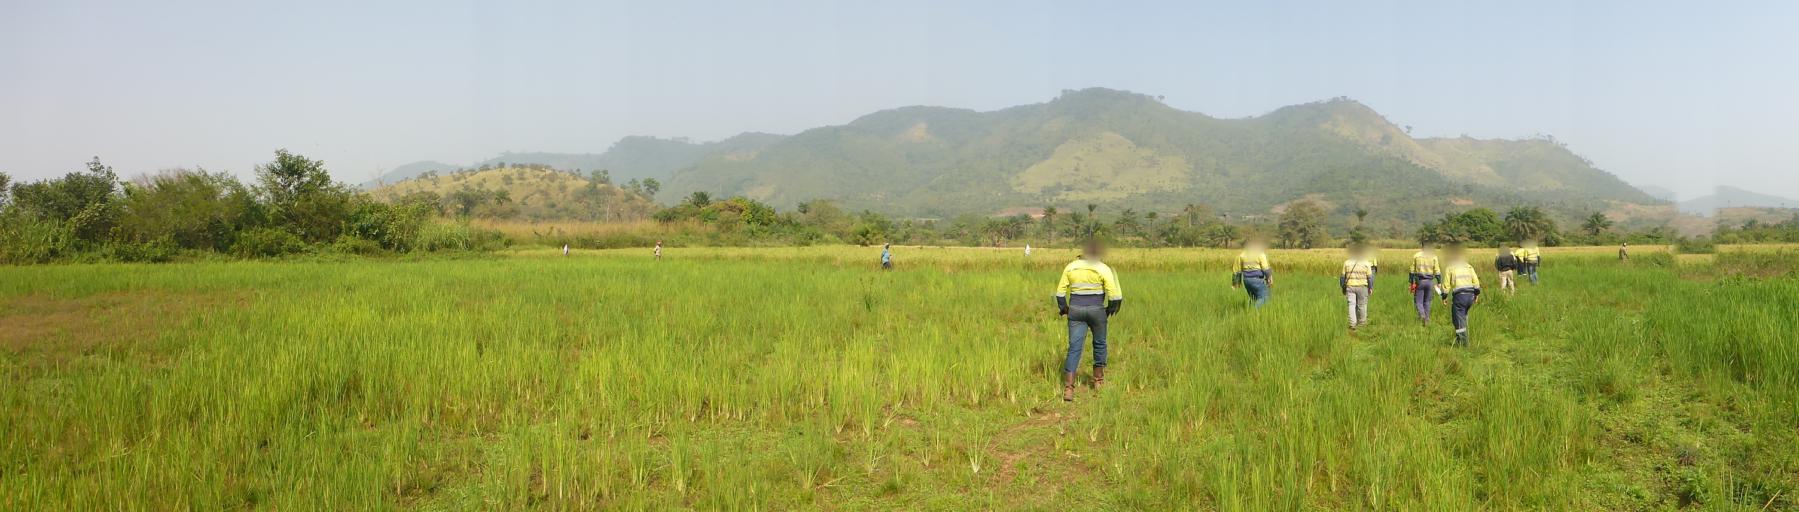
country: SL
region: Northern Province
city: Bumbuna
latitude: 8.9280
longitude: -11.7501
